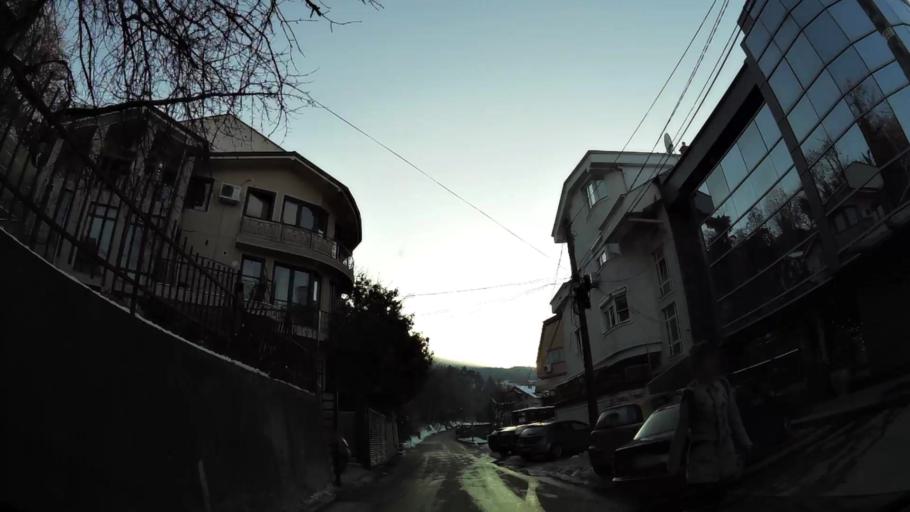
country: MK
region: Karpos
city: Skopje
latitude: 41.9929
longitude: 21.4076
